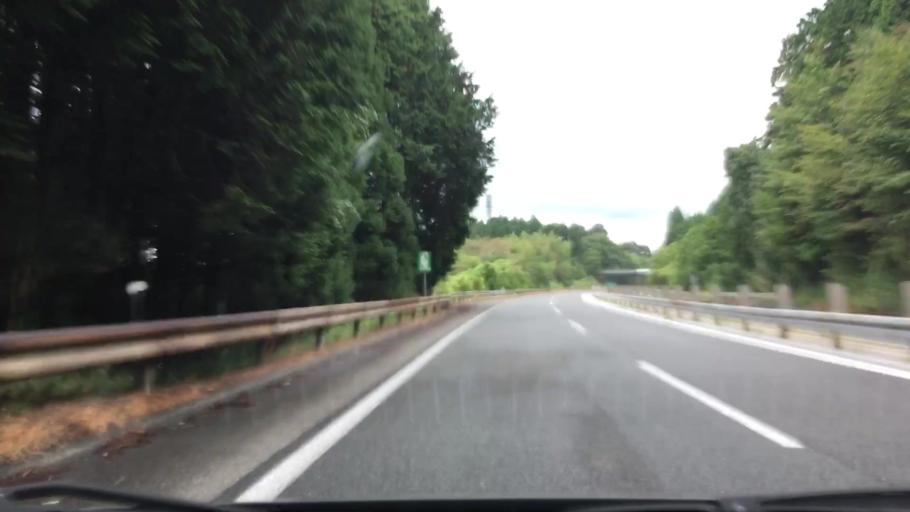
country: JP
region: Okayama
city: Niimi
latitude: 34.9292
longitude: 133.3267
